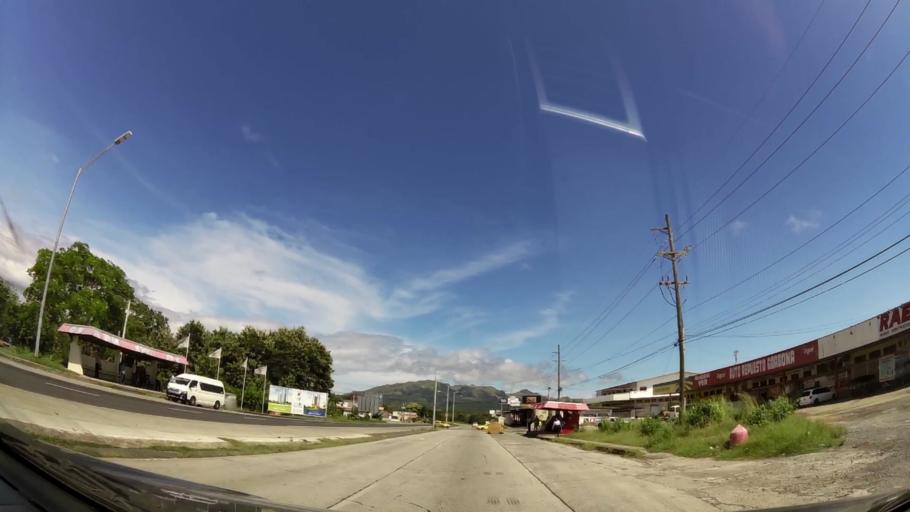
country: PA
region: Panama
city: Chame
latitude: 8.5645
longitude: -79.8914
